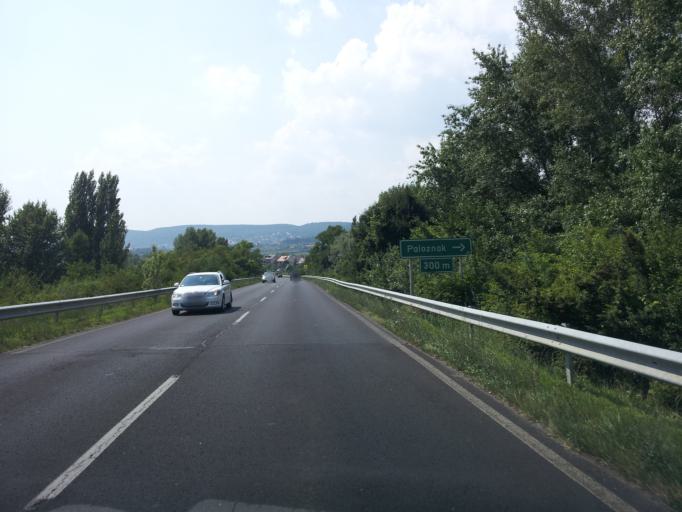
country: HU
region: Veszprem
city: Csopak
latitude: 46.9788
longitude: 17.9496
